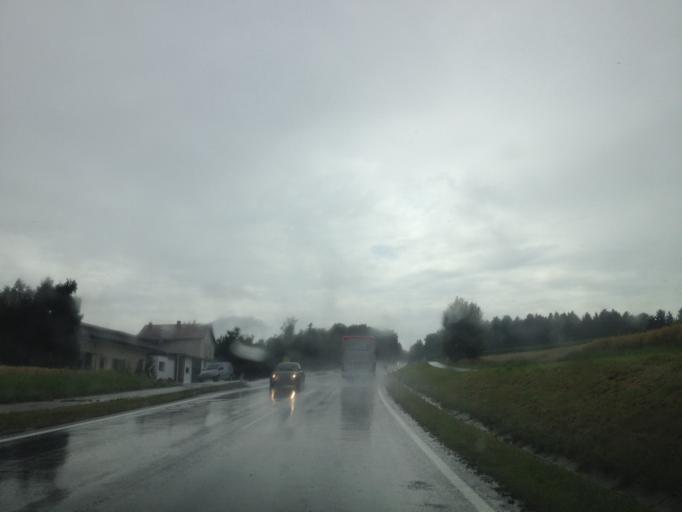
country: AT
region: Burgenland
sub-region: Politischer Bezirk Oberwart
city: Oberwart
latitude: 47.2806
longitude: 16.1770
